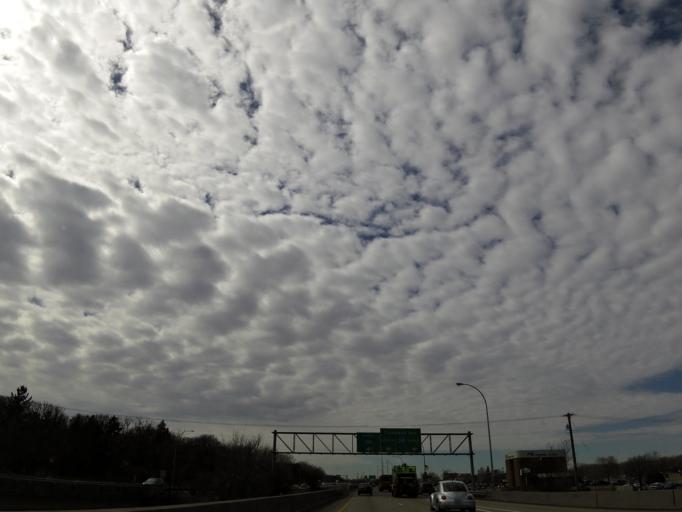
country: US
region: Minnesota
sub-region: Ramsey County
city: Roseville
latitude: 45.0104
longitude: -93.1760
